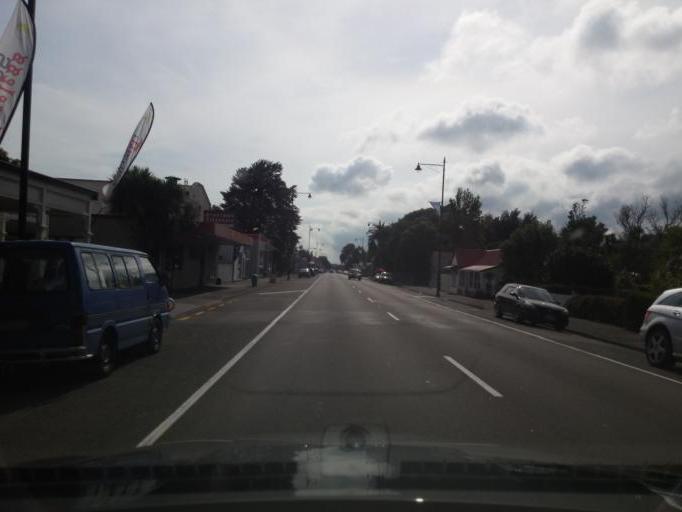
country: NZ
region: Wellington
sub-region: Masterton District
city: Masterton
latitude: -41.0821
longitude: 175.4583
